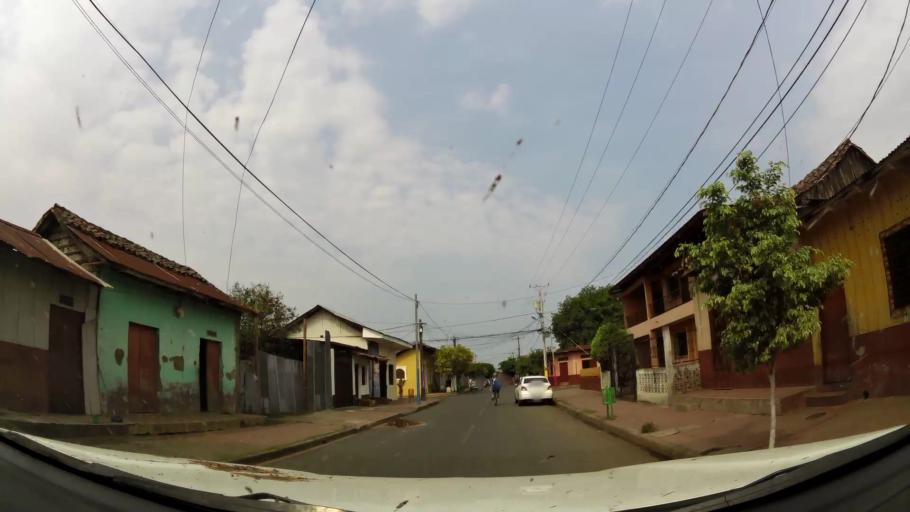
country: NI
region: Masaya
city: Masaya
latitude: 11.9749
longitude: -86.1013
